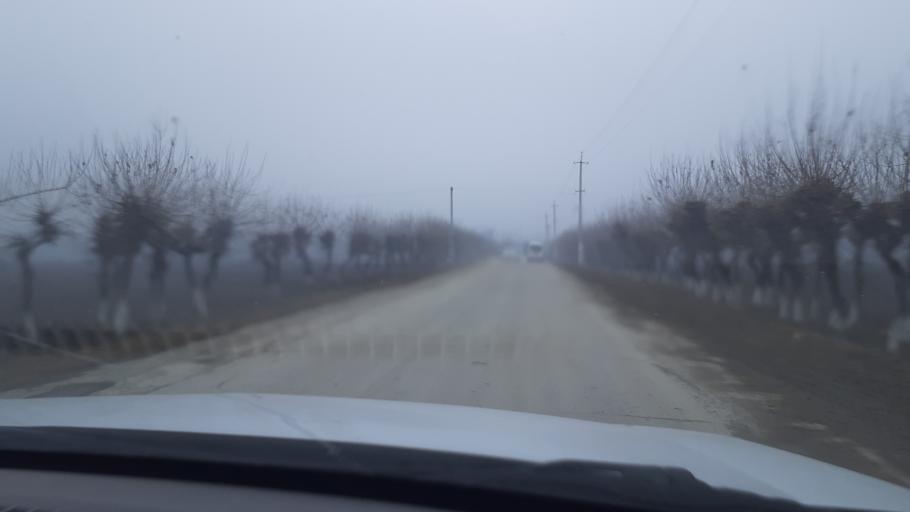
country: UZ
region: Namangan
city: Haqqulobod
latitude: 40.9005
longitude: 71.9988
